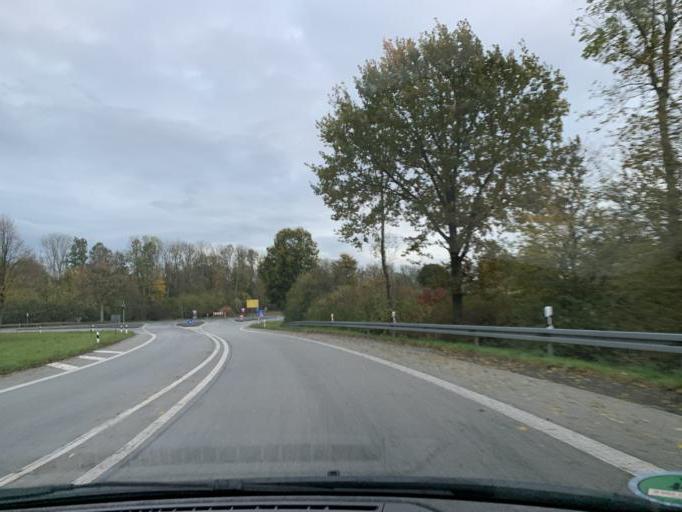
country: DE
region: North Rhine-Westphalia
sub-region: Regierungsbezirk Koln
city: Titz
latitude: 51.0068
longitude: 6.4053
